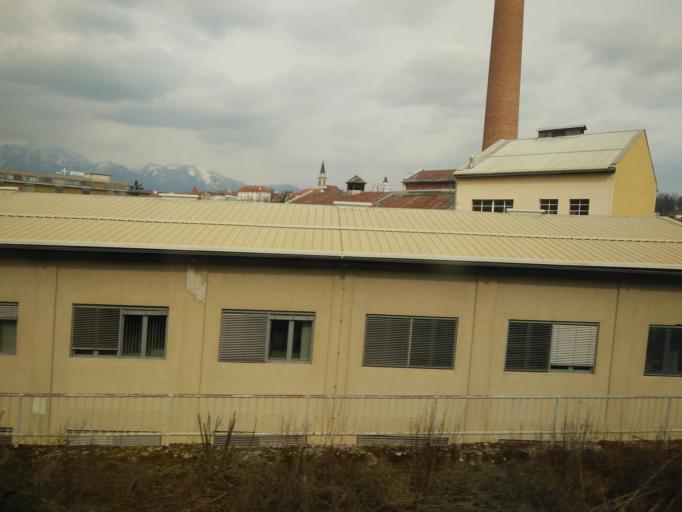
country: SI
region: Kranj
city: Kranj
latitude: 46.2346
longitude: 14.3498
